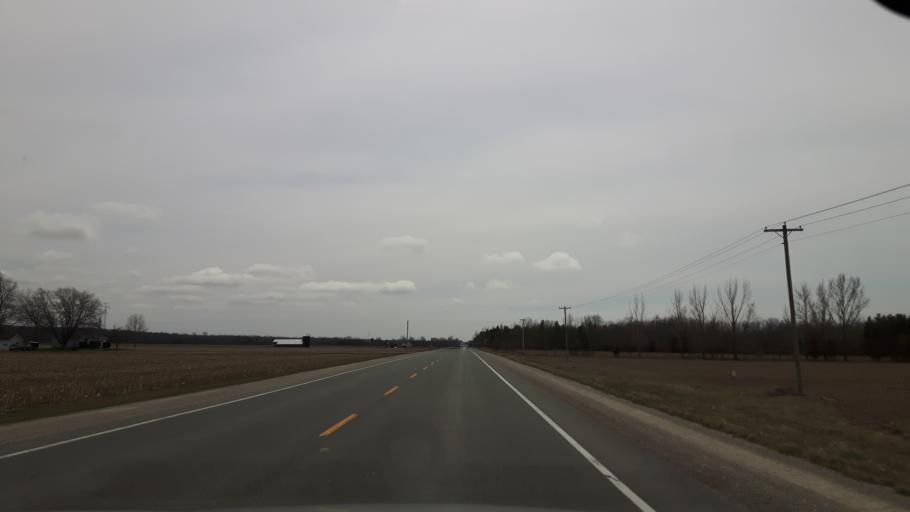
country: CA
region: Ontario
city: Goderich
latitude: 43.6280
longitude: -81.7057
